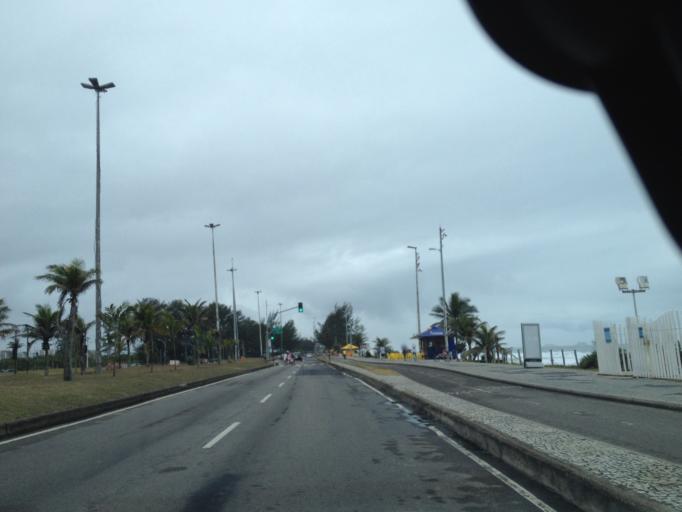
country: BR
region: Rio de Janeiro
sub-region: Nilopolis
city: Nilopolis
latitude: -23.0229
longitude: -43.4491
